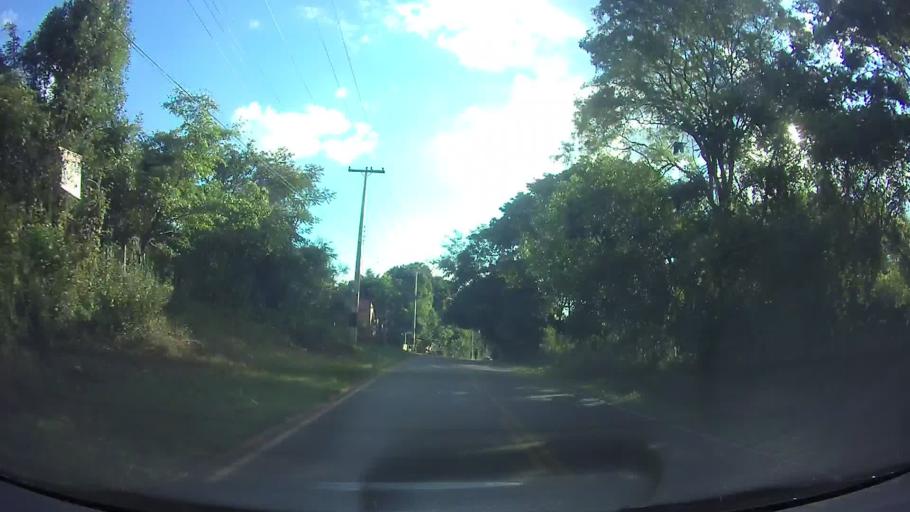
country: PY
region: Central
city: Aregua
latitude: -25.2678
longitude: -57.4257
